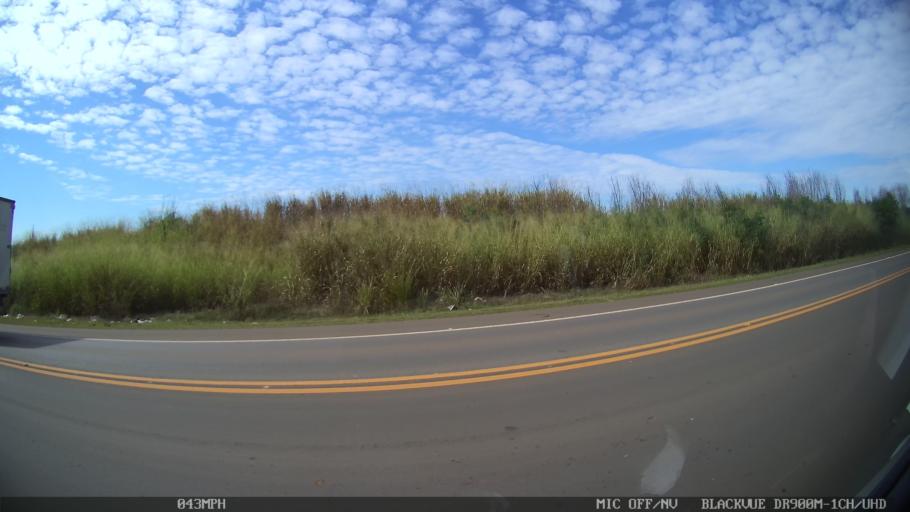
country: BR
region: Sao Paulo
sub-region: Santa Barbara D'Oeste
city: Santa Barbara d'Oeste
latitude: -22.7202
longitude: -47.4266
